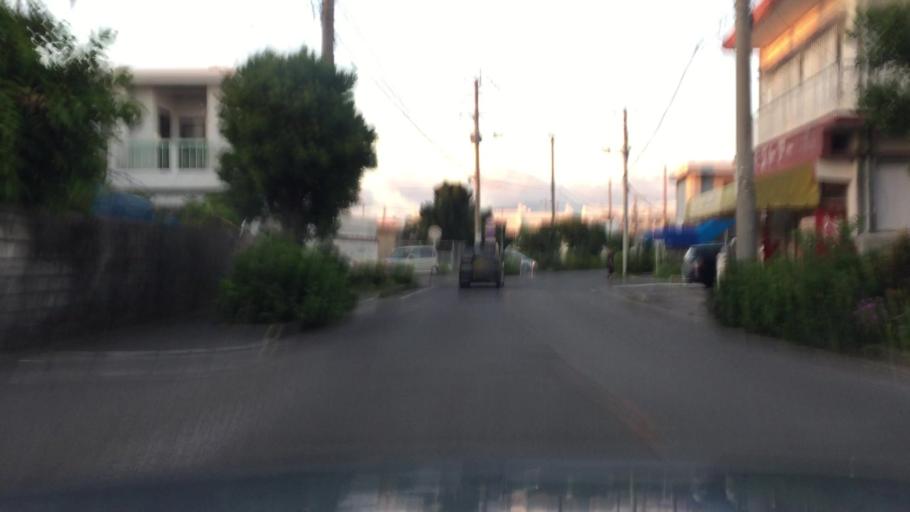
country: JP
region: Okinawa
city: Ishigaki
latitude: 24.3479
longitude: 124.1627
